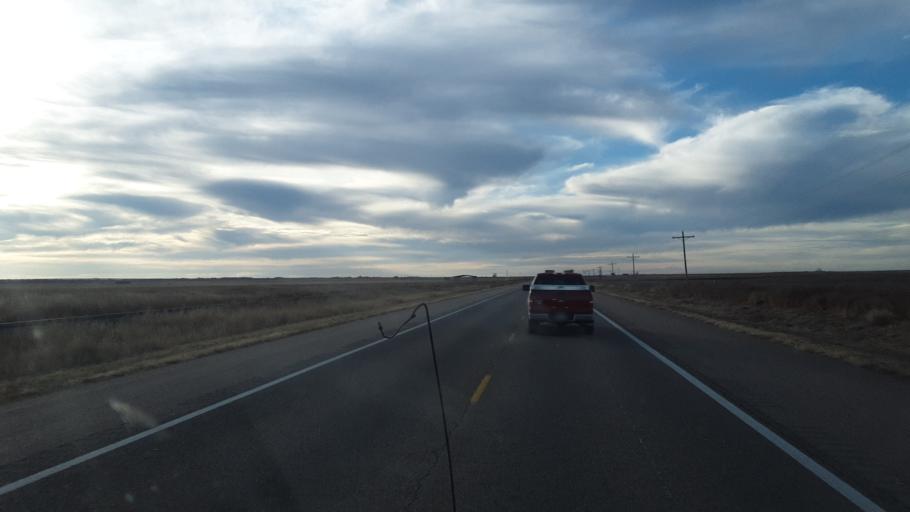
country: US
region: Kansas
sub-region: Hamilton County
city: Syracuse
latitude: 37.9566
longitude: -101.6438
